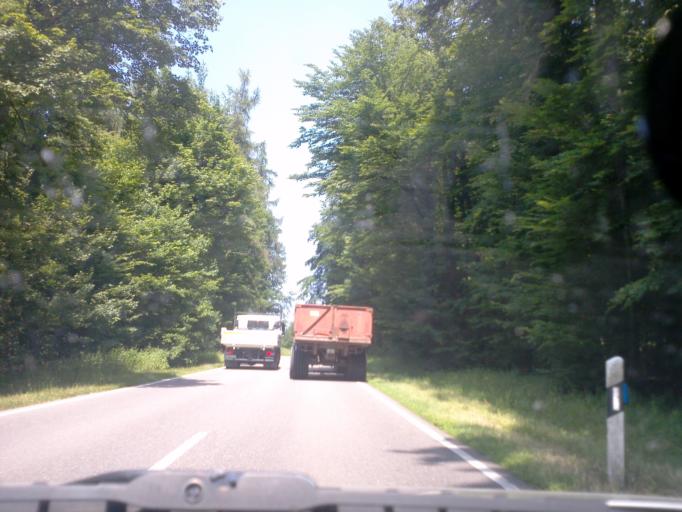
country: DE
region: Baden-Wuerttemberg
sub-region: Karlsruhe Region
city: Eisingen
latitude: 49.0010
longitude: 8.6643
